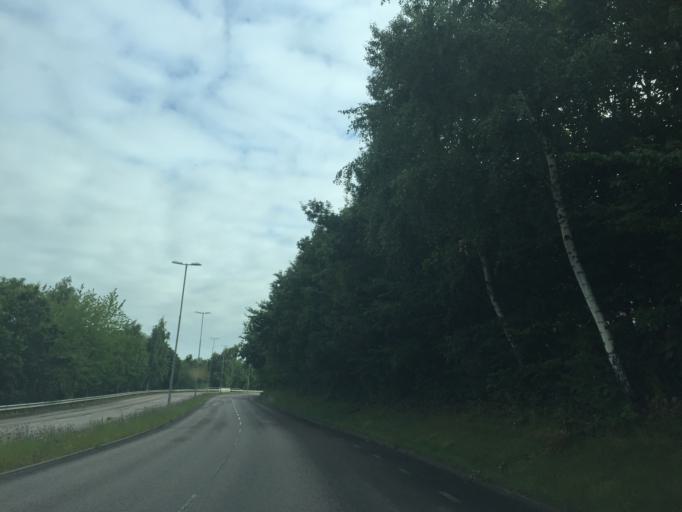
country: SE
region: Skane
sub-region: Angelholms Kommun
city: AEngelholm
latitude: 56.2394
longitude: 12.8665
